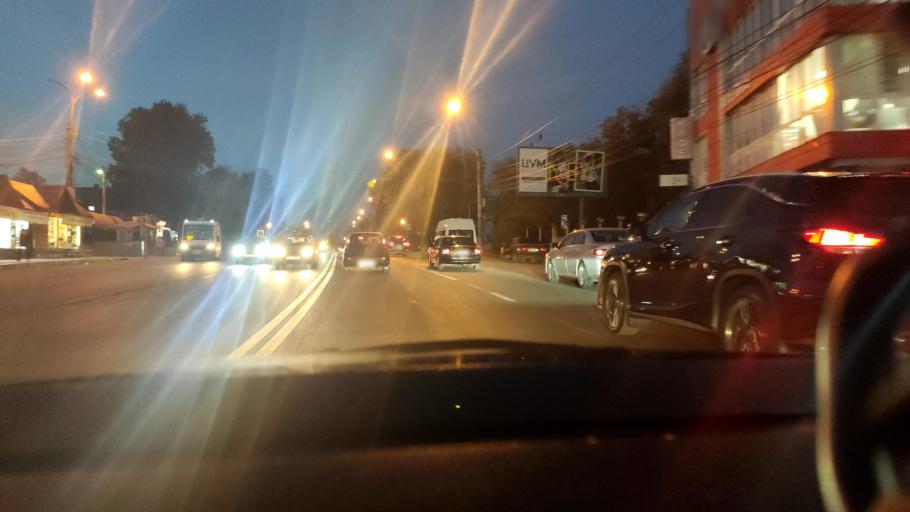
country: RU
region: Voronezj
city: Voronezh
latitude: 51.6984
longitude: 39.2317
